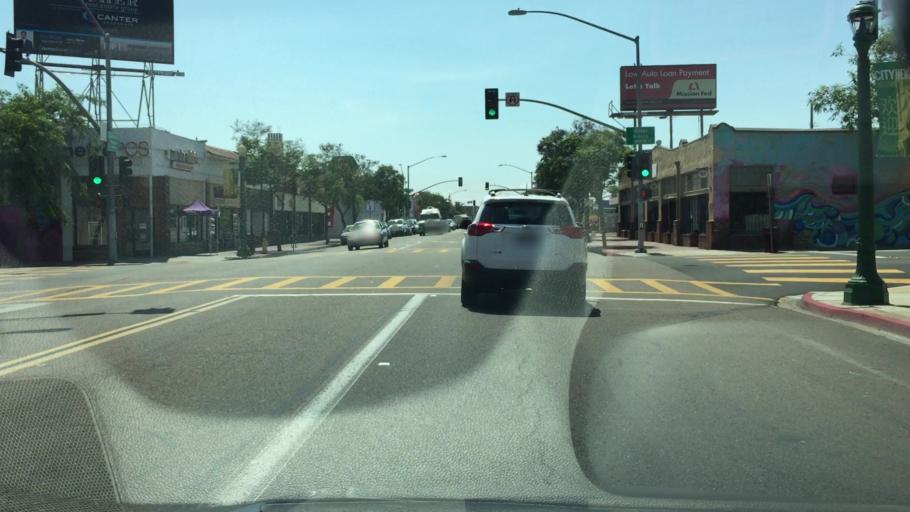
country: US
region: California
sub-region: San Diego County
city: San Diego
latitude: 32.7498
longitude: -117.1166
